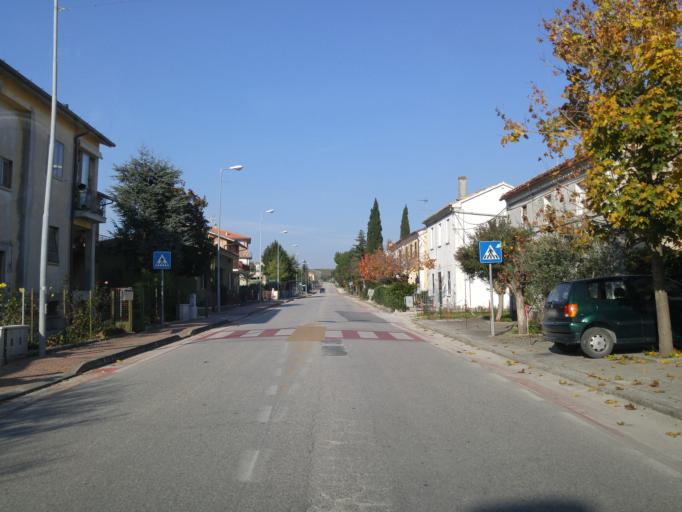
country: IT
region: The Marches
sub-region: Provincia di Pesaro e Urbino
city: Piagge
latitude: 43.7353
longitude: 12.9694
